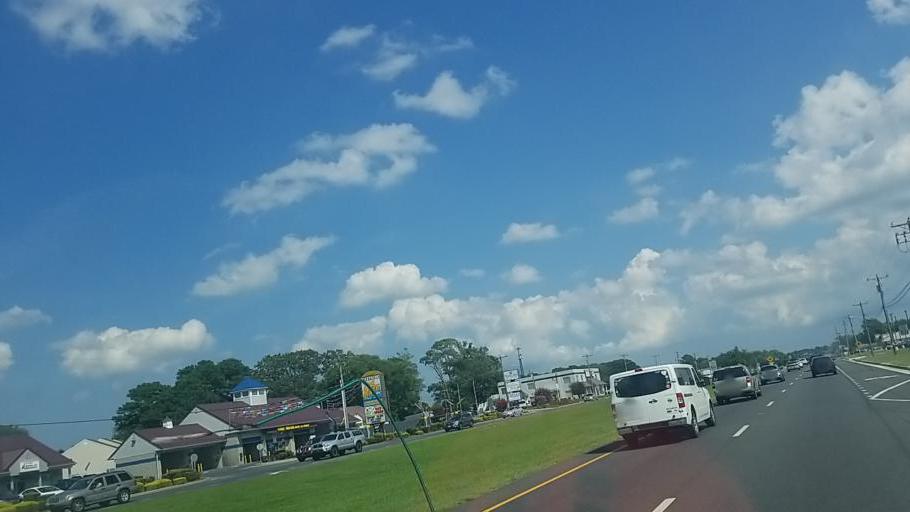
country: US
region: Delaware
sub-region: Sussex County
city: Millsboro
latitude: 38.5910
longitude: -75.3053
